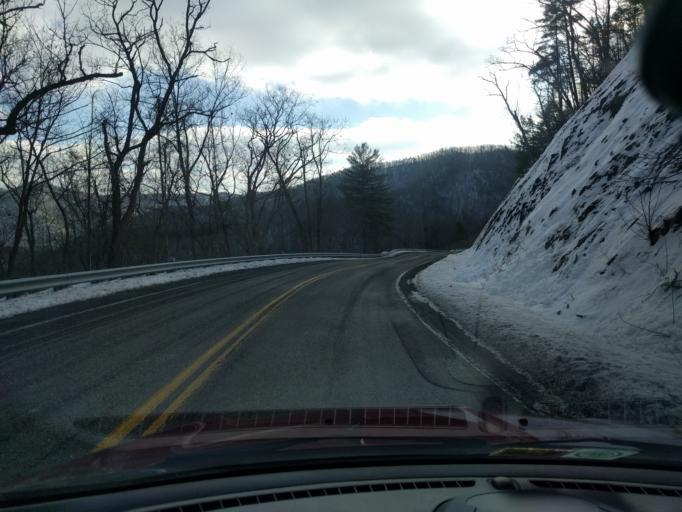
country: US
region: Virginia
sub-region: Bath County
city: Warm Springs
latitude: 38.1222
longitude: -79.9411
